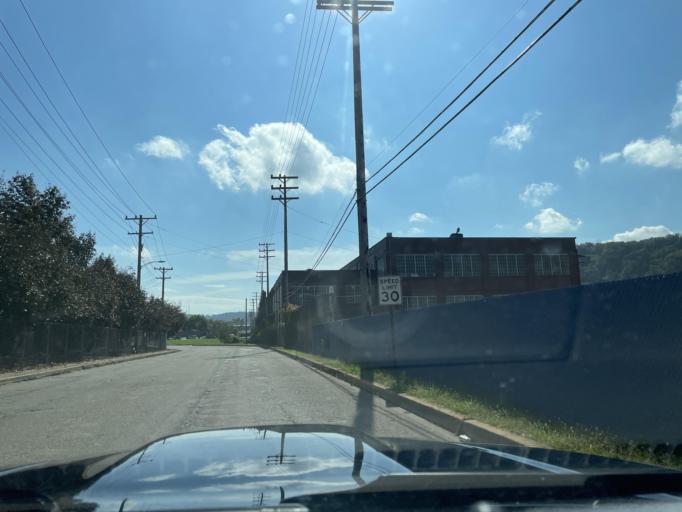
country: US
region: Pennsylvania
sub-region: Westmoreland County
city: New Kensington
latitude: 40.5675
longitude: -79.7697
